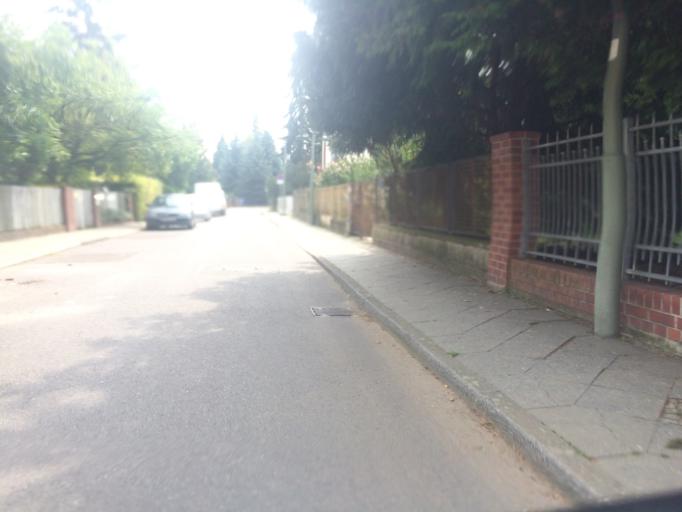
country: DE
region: Berlin
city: Heinersdorf
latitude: 52.5685
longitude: 13.4329
